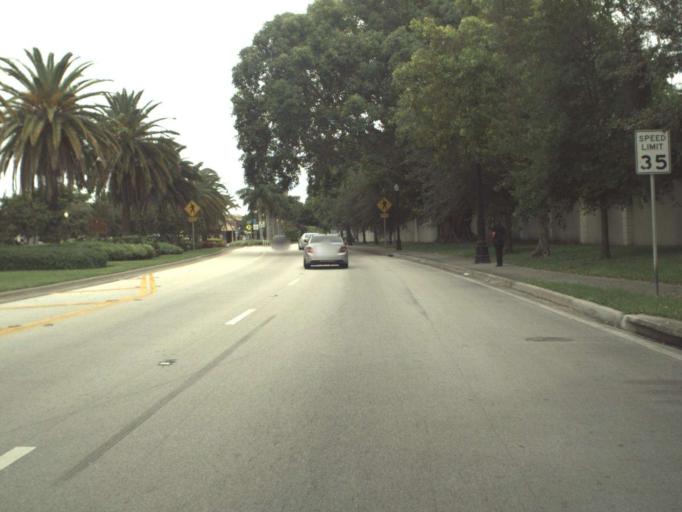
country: US
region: Florida
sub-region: Miami-Dade County
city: Allapattah
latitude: 25.8184
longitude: -80.1878
